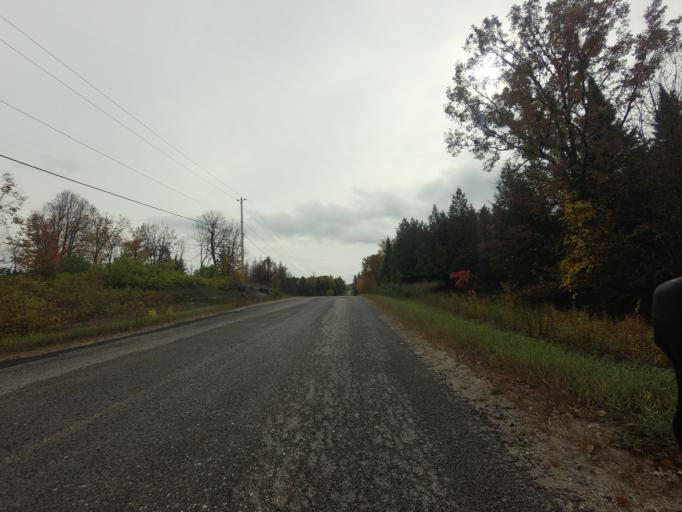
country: CA
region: Ontario
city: Perth
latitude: 45.1200
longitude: -76.5182
